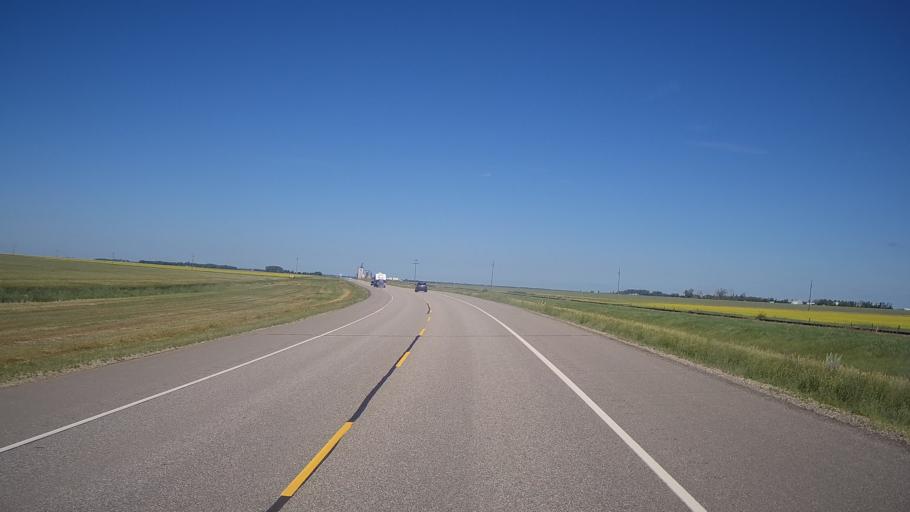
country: CA
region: Manitoba
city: Portage la Prairie
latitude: 50.0609
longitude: -98.4759
